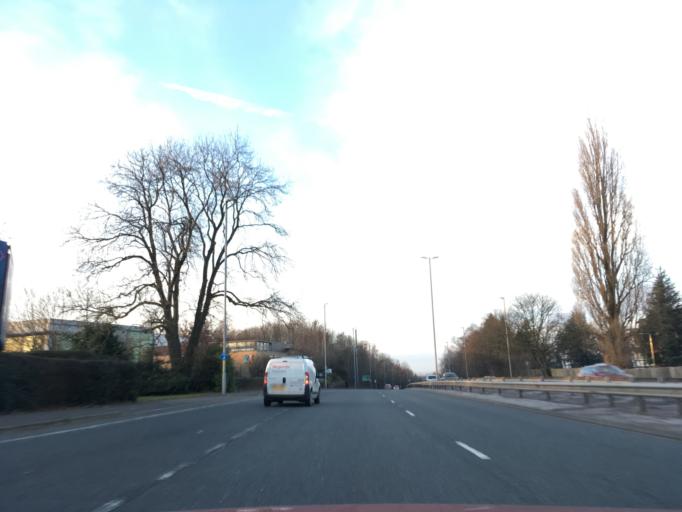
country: GB
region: England
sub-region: Borough of Stockport
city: Cheadle Hulme
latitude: 53.3809
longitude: -2.2199
